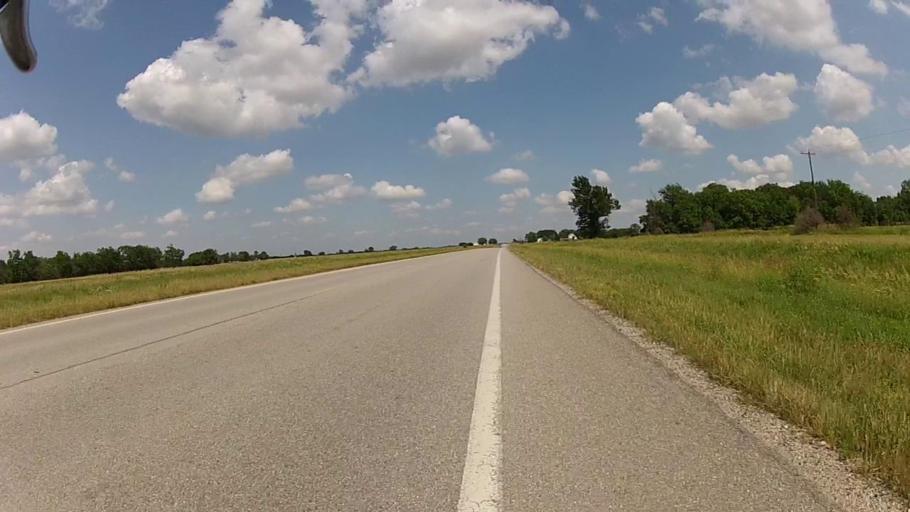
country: US
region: Kansas
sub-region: Labette County
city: Oswego
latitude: 37.1938
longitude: -95.1839
